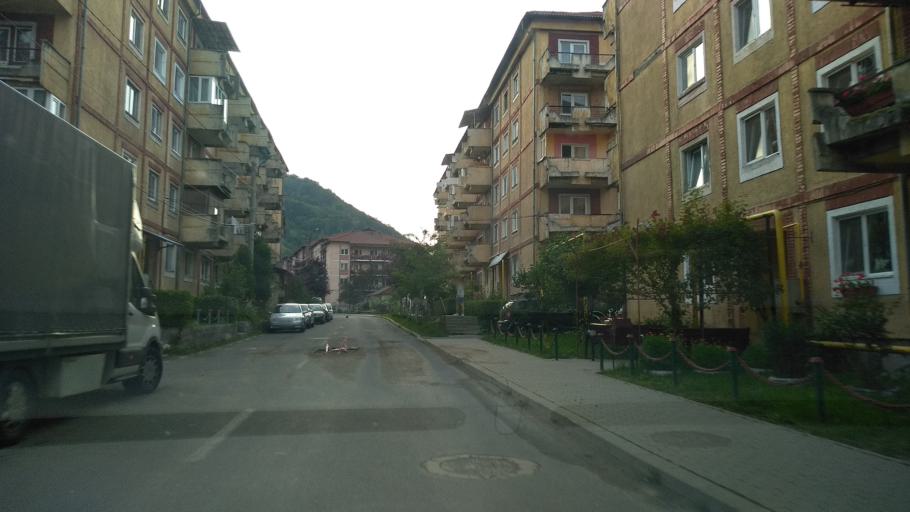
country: RO
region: Hunedoara
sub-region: Comuna Aninoasa
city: Aninoasa
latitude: 45.4073
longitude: 23.3179
